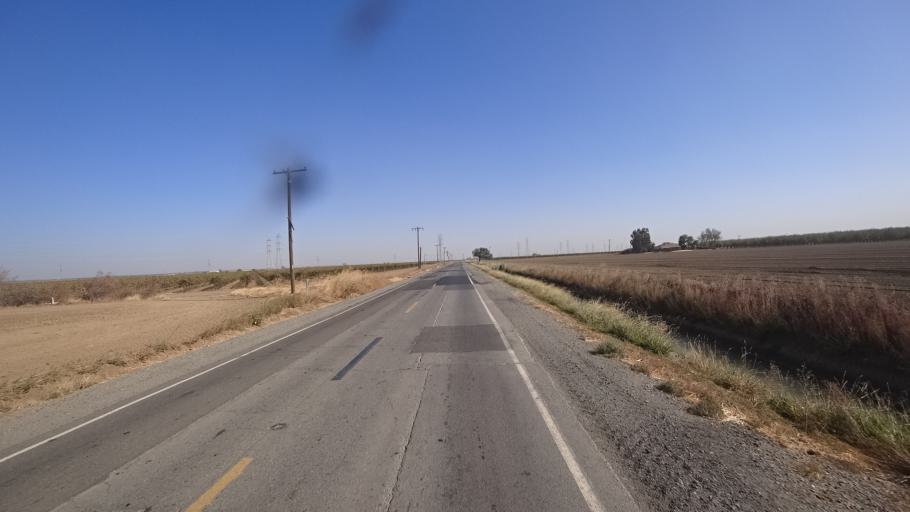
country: US
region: California
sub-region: Yolo County
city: Esparto
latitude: 38.7289
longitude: -121.9789
